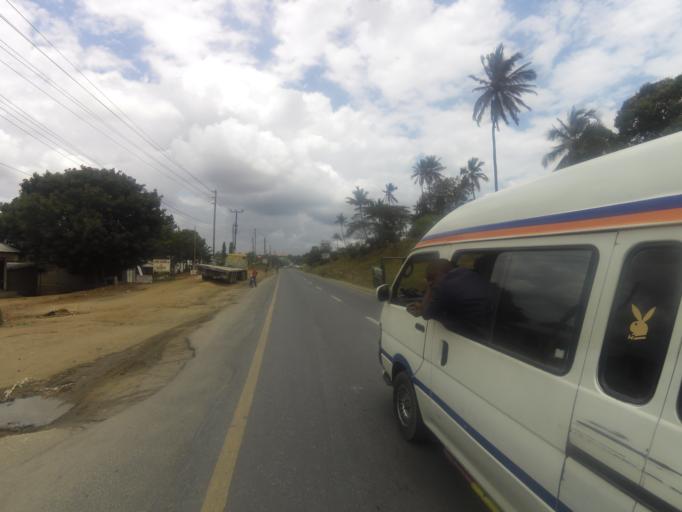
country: TZ
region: Pwani
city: Vikindu
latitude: -6.9512
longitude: 39.2820
